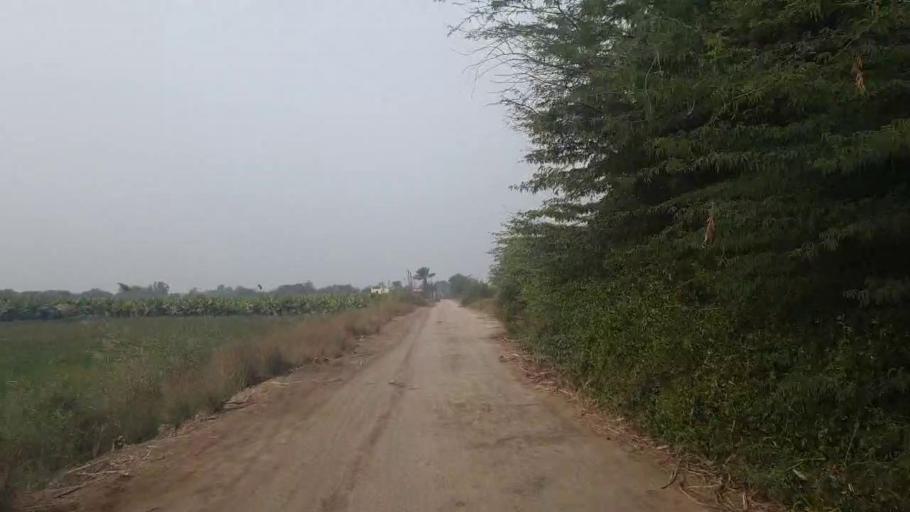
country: PK
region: Sindh
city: Tando Adam
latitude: 25.8107
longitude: 68.7184
